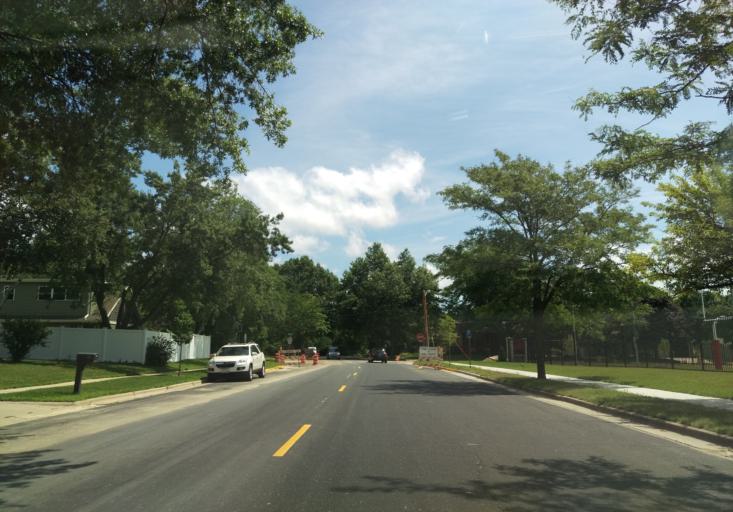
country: US
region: Wisconsin
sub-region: Dane County
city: Middleton
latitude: 43.1058
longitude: -89.5032
